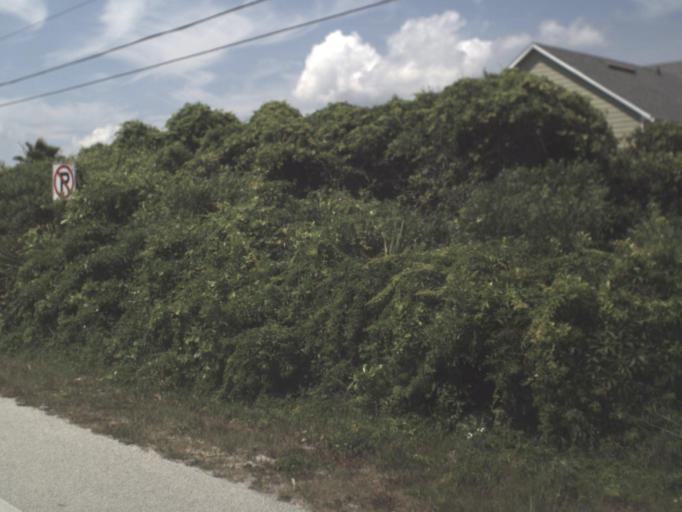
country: US
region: Florida
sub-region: Saint Johns County
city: Villano Beach
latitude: 29.9464
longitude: -81.3027
